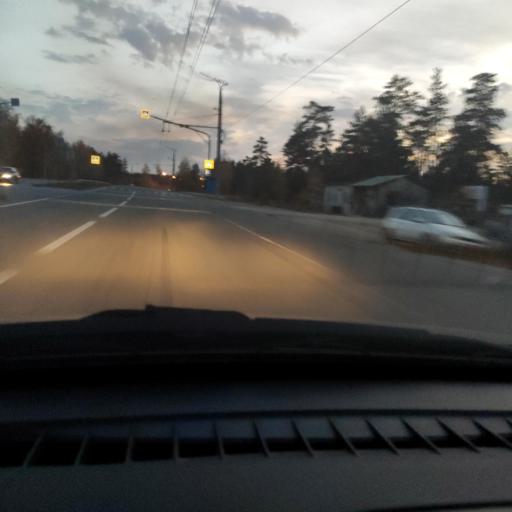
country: RU
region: Samara
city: Zhigulevsk
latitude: 53.5319
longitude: 49.5551
